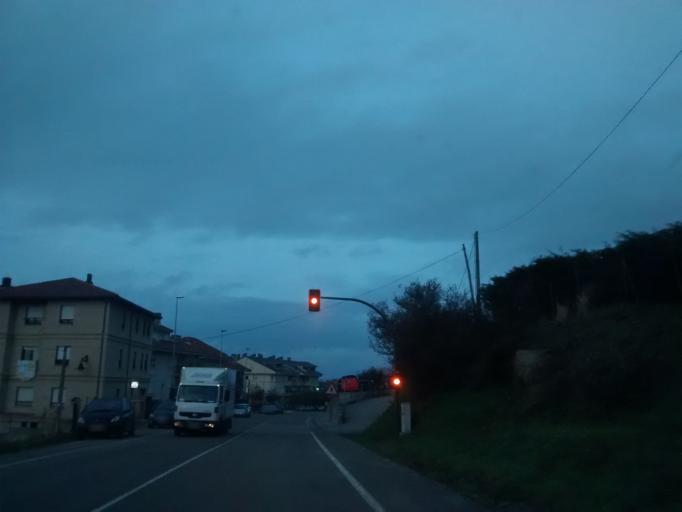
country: ES
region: Cantabria
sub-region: Provincia de Cantabria
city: Santa Cruz de Bezana
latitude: 43.4570
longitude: -3.9322
